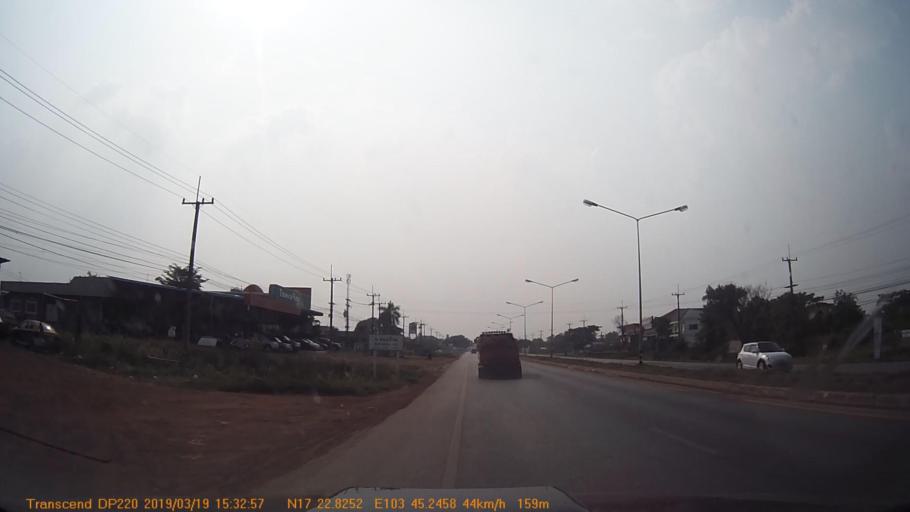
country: TH
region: Sakon Nakhon
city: Phang Khon
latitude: 17.3805
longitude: 103.7539
